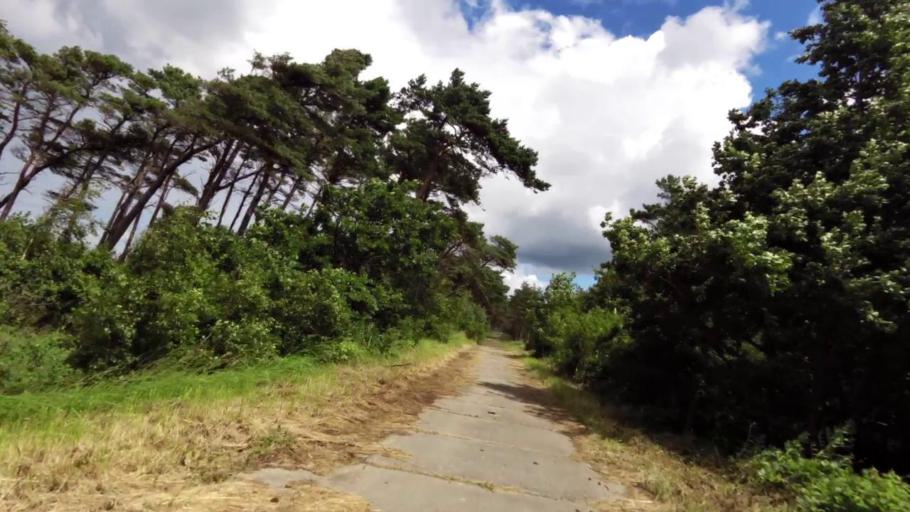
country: PL
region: West Pomeranian Voivodeship
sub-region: Powiat slawienski
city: Darlowo
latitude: 54.4959
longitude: 16.4475
